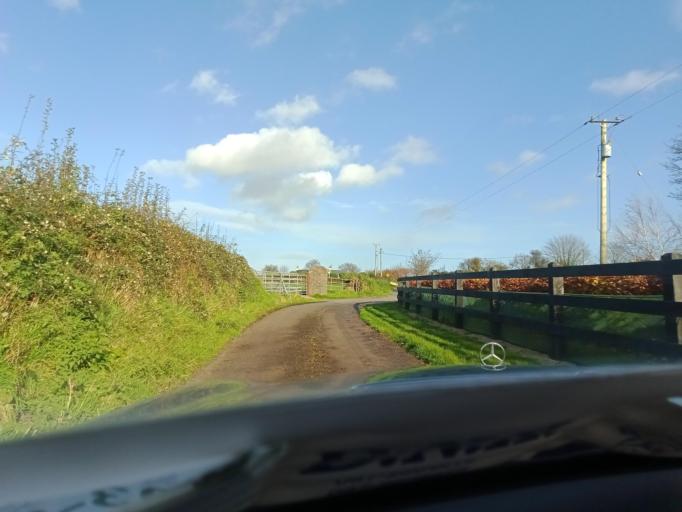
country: IE
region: Munster
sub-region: Waterford
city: Portlaw
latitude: 52.3138
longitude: -7.2953
